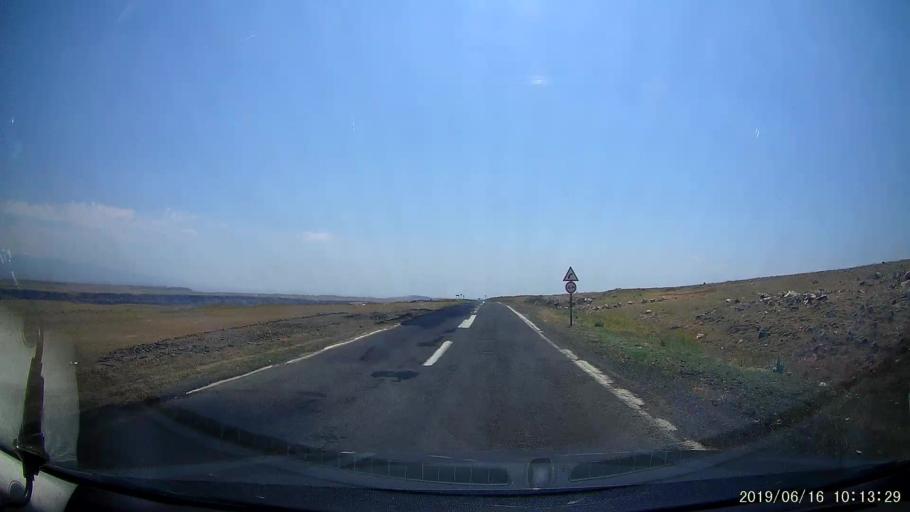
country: TR
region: Igdir
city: Tuzluca
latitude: 40.1924
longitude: 43.6436
